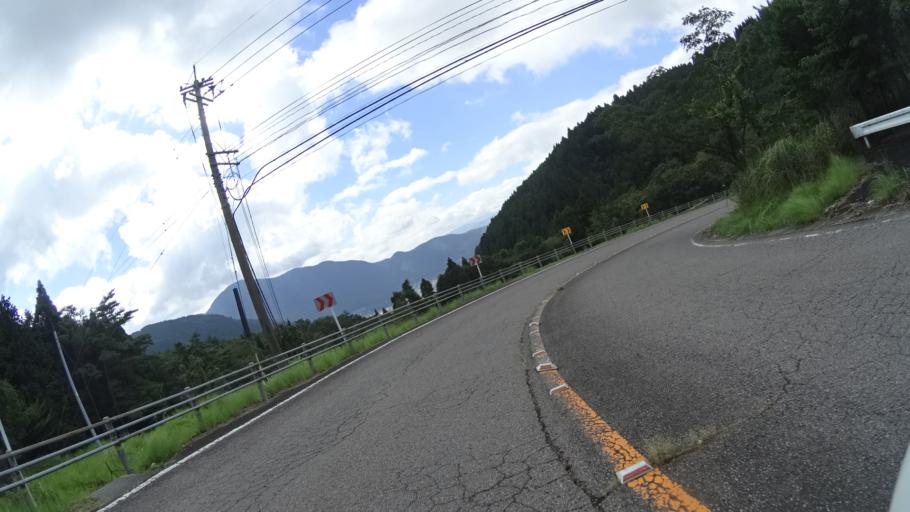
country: JP
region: Oita
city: Beppu
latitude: 33.2825
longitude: 131.3703
